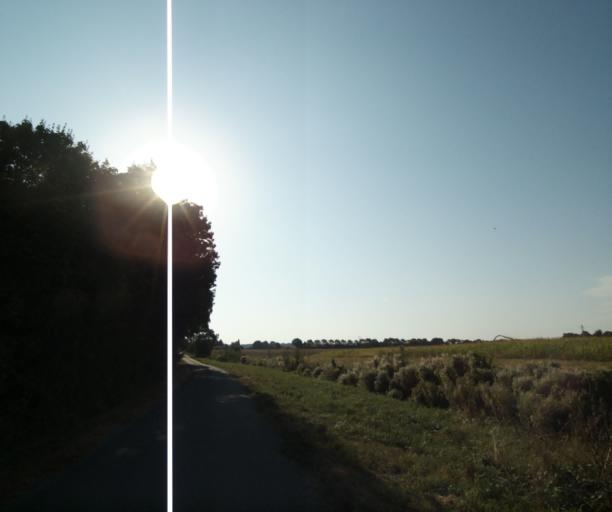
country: FR
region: Poitou-Charentes
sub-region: Departement de la Charente-Maritime
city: Muron
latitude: 45.9854
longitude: -0.8267
